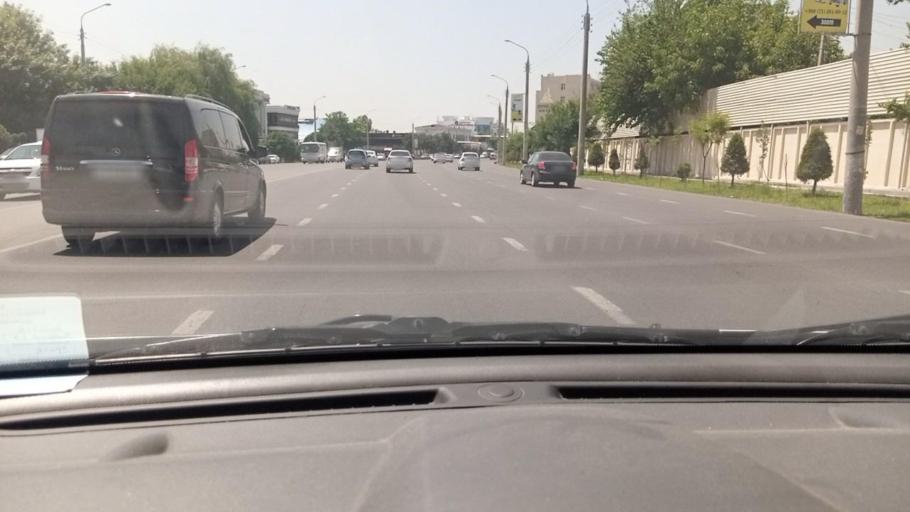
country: UZ
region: Toshkent Shahri
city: Tashkent
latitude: 41.2718
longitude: 69.2670
